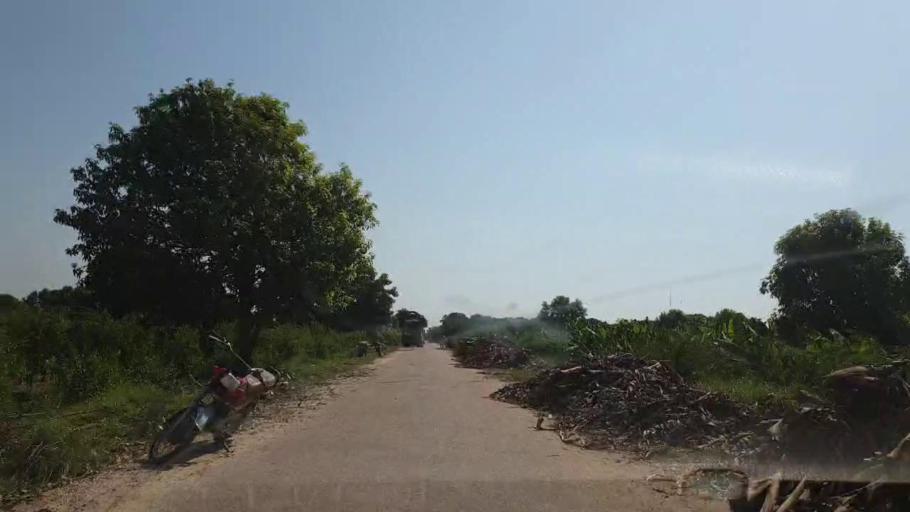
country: PK
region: Sindh
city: Tando Jam
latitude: 25.4159
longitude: 68.5821
